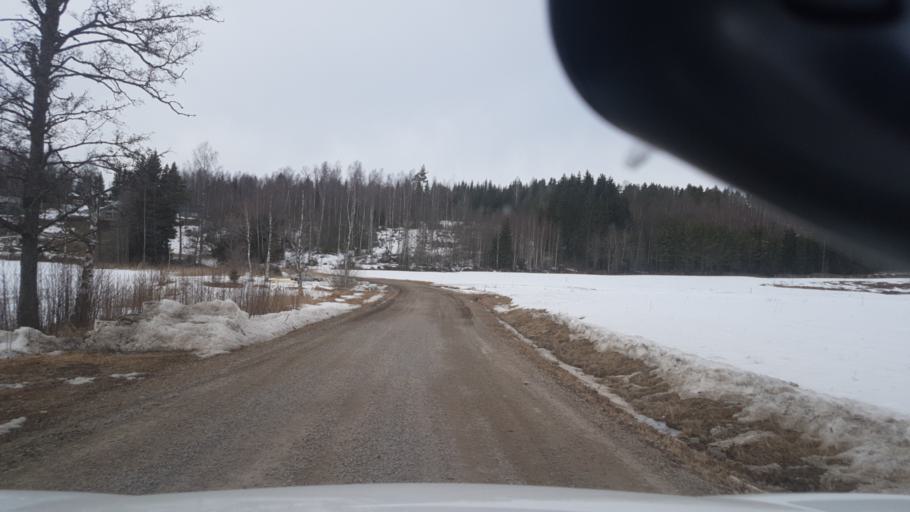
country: SE
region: Vaermland
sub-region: Eda Kommun
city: Amotfors
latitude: 59.8254
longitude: 12.4453
